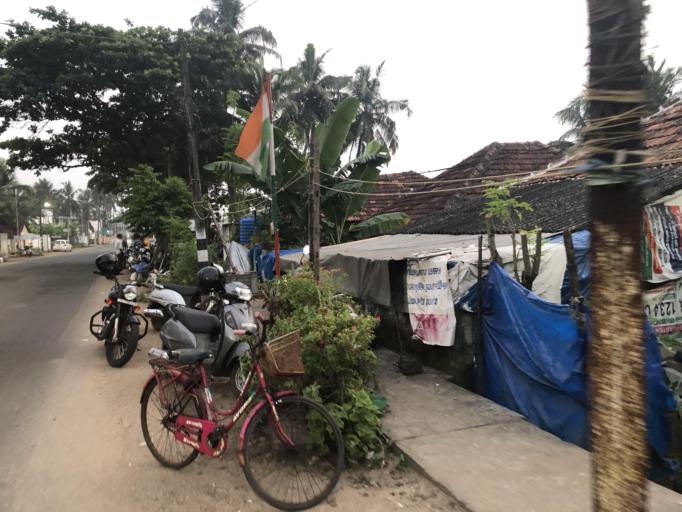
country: IN
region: Kerala
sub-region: Kozhikode
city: Kozhikode
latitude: 11.2414
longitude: 75.7742
